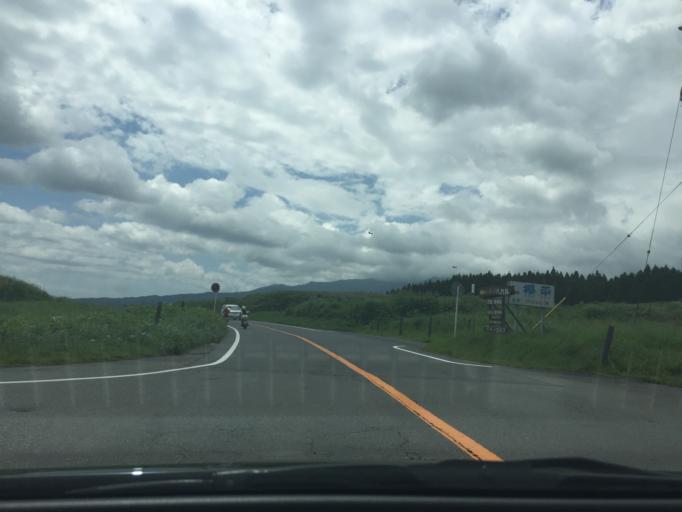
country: JP
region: Shizuoka
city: Gotemba
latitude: 35.2773
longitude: 138.8750
